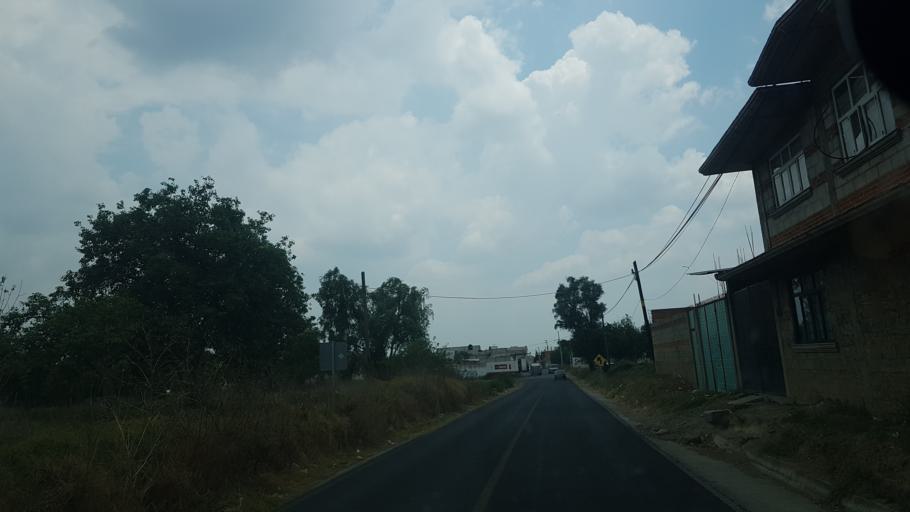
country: MX
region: Puebla
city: Huejotzingo
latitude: 19.1586
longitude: -98.4205
